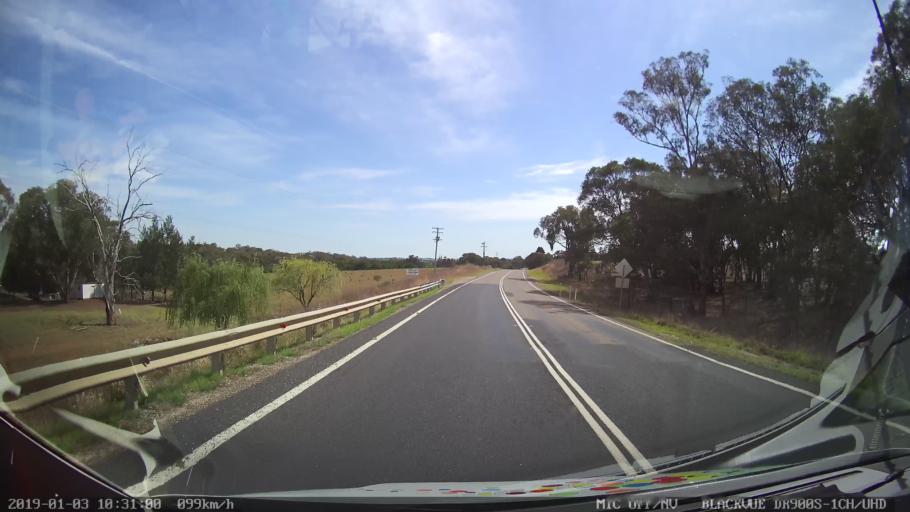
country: AU
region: New South Wales
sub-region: Young
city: Young
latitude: -34.3553
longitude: 148.2730
